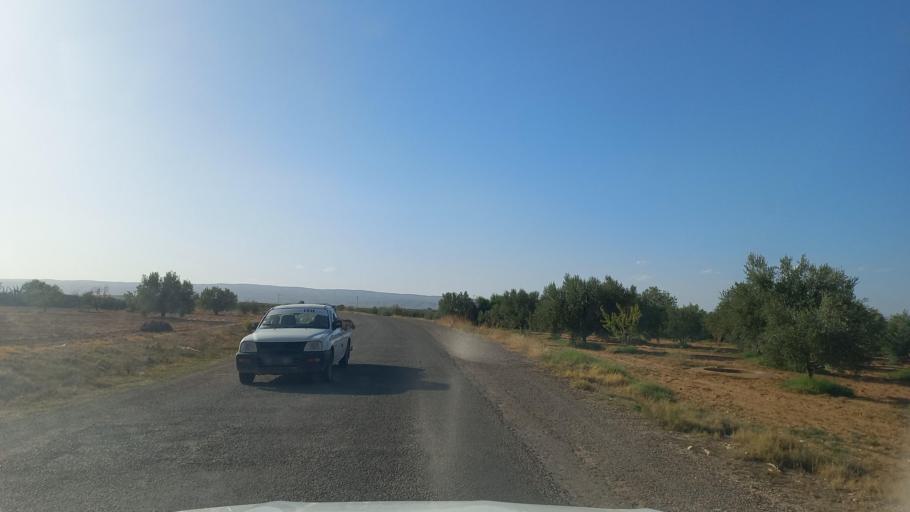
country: TN
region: Al Qasrayn
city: Kasserine
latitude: 35.2588
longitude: 9.0330
